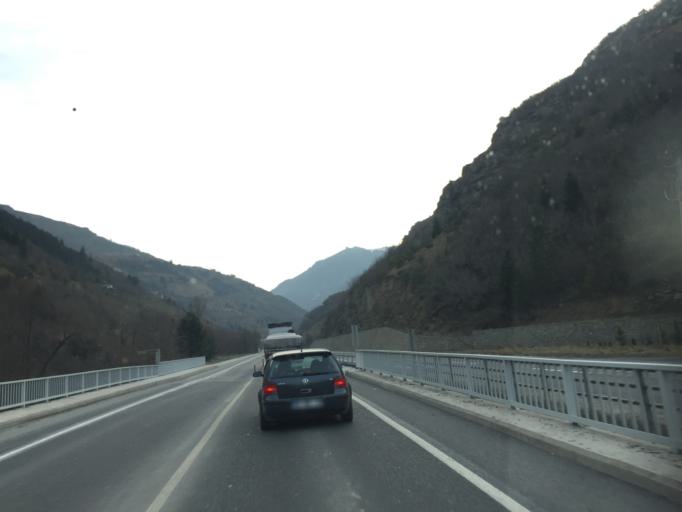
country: TR
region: Trabzon
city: Macka
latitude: 40.7958
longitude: 39.5839
